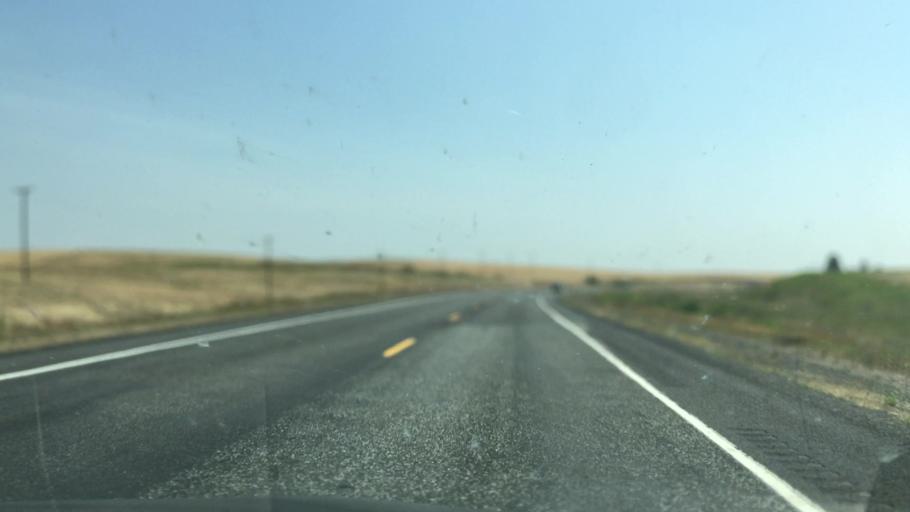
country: US
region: Idaho
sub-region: Lewis County
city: Nezperce
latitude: 46.2295
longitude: -116.4493
